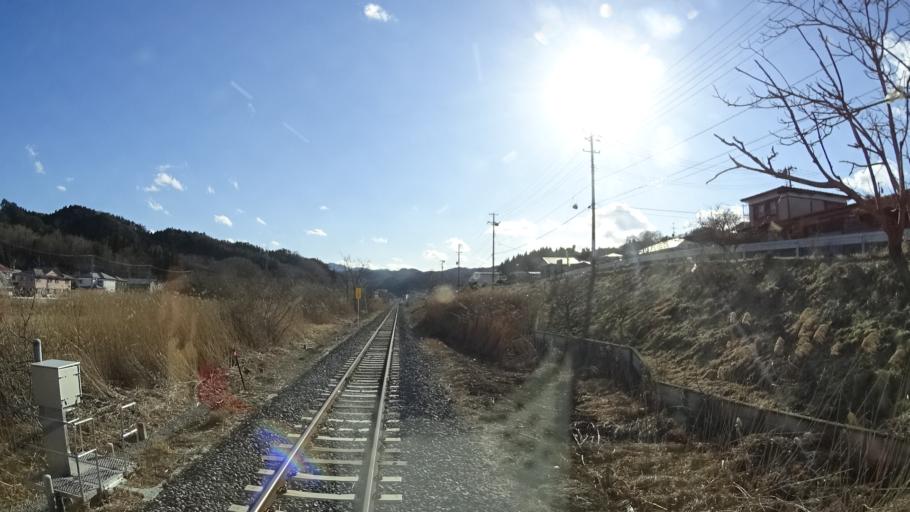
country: JP
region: Iwate
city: Miyako
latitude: 39.6204
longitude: 141.9483
